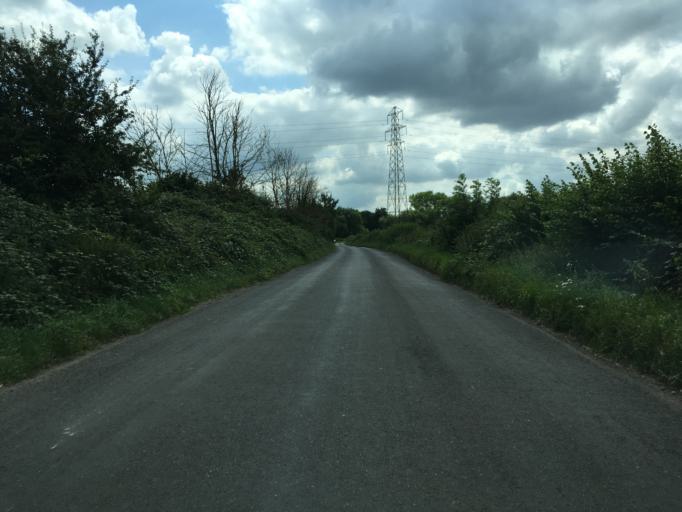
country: GB
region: England
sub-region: Gloucestershire
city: Gloucester
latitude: 51.8899
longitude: -2.2532
